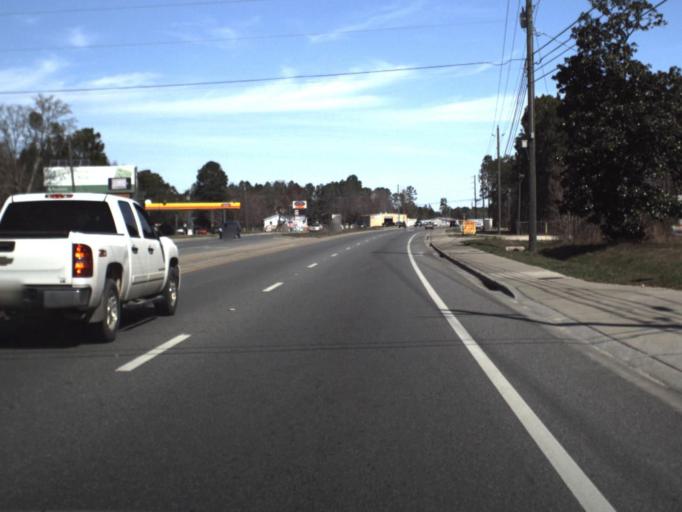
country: US
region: Florida
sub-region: Bay County
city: Lynn Haven
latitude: 30.2726
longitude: -85.6402
